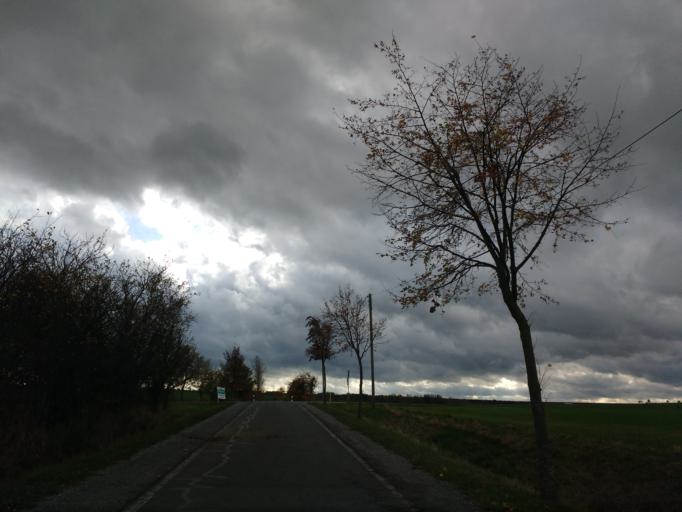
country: DE
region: Thuringia
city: Worbis
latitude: 51.4082
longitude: 10.3583
